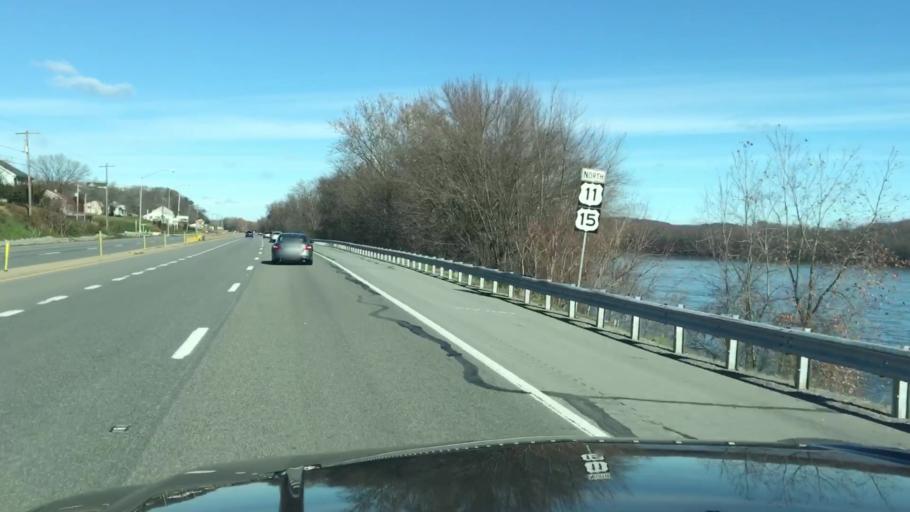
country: US
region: Pennsylvania
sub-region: Snyder County
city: Selinsgrove
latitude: 40.7298
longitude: -76.8555
